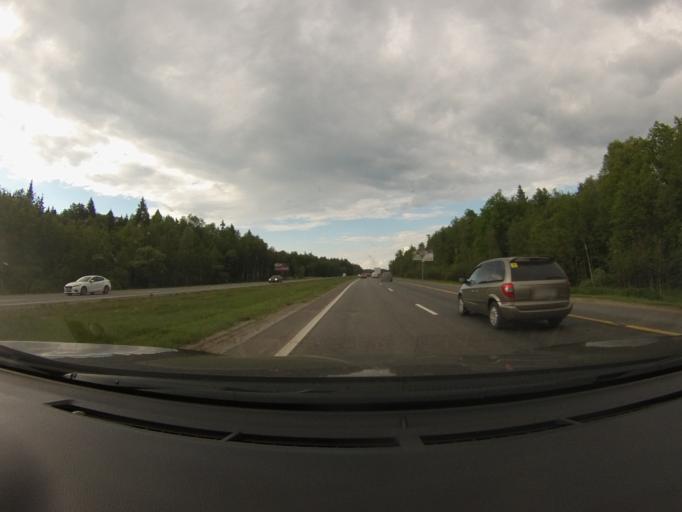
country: RU
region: Moskovskaya
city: Danki
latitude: 54.9685
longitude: 37.5297
